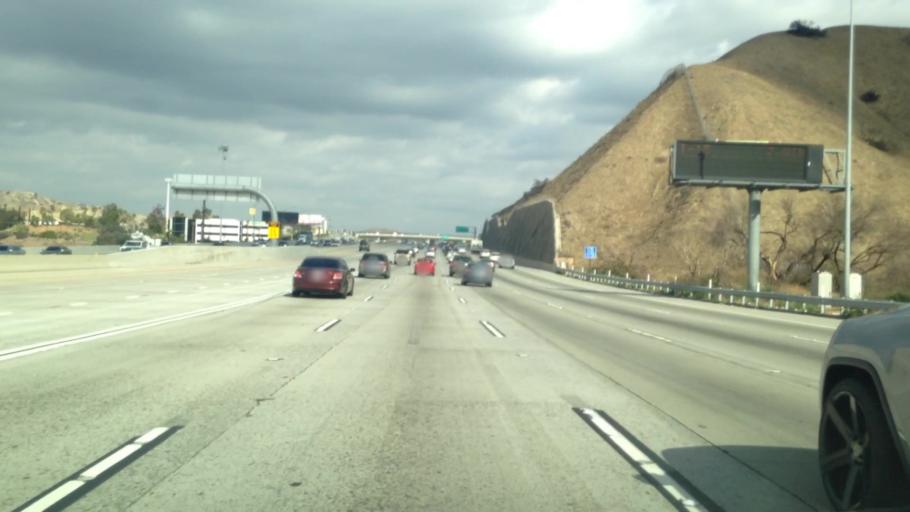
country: US
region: California
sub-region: Riverside County
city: Corona
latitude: 33.8733
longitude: -117.6637
